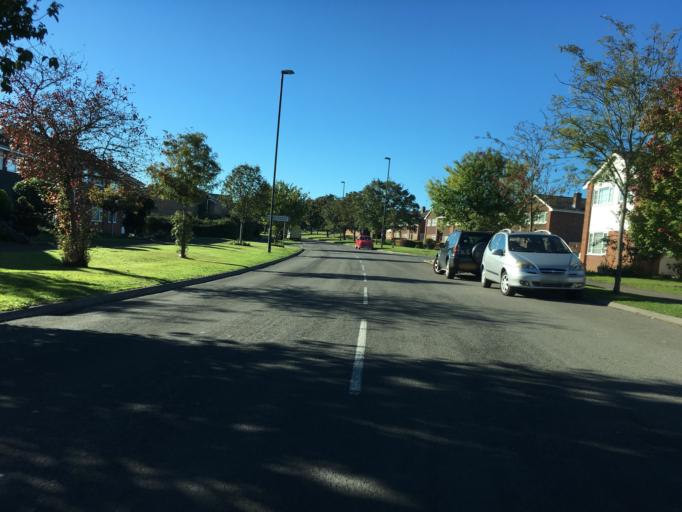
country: GB
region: England
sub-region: South Gloucestershire
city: Chipping Sodbury
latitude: 51.5337
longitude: -2.4030
